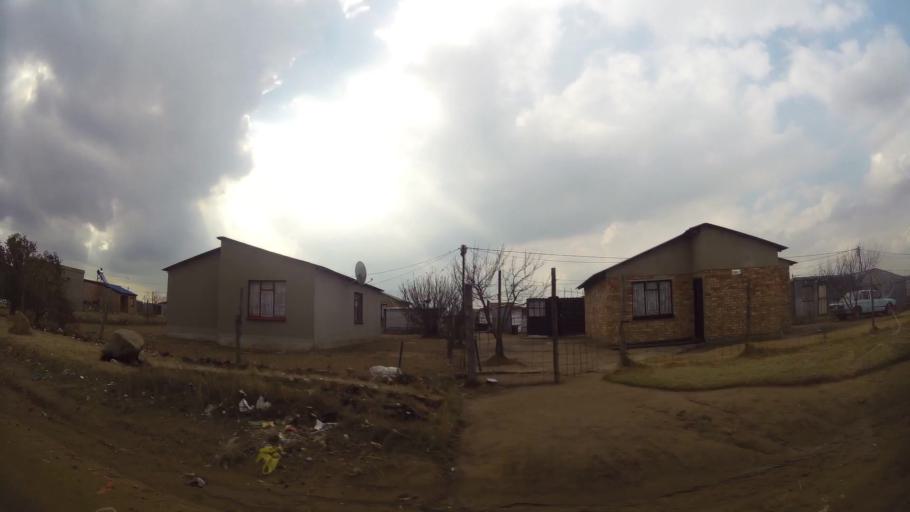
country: ZA
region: Orange Free State
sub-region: Fezile Dabi District Municipality
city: Sasolburg
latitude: -26.8630
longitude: 27.8934
